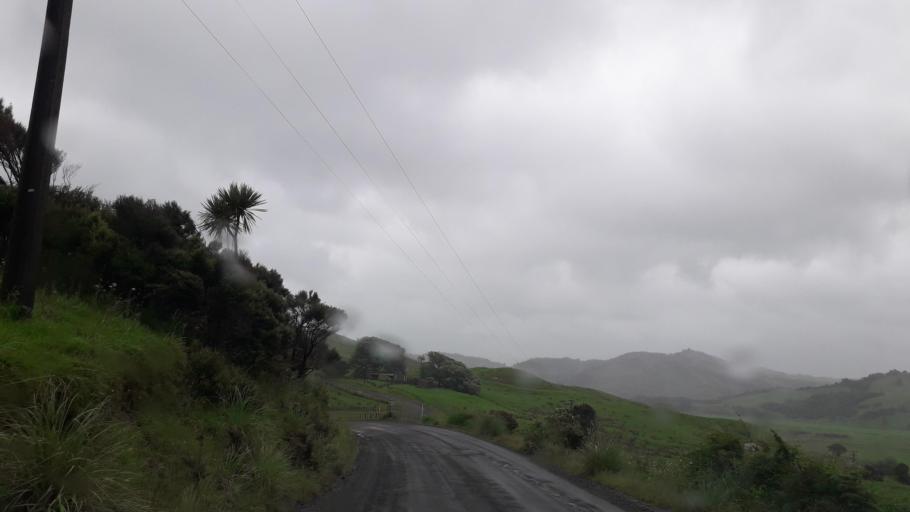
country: NZ
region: Northland
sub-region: Far North District
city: Kaitaia
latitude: -35.4128
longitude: 173.3655
